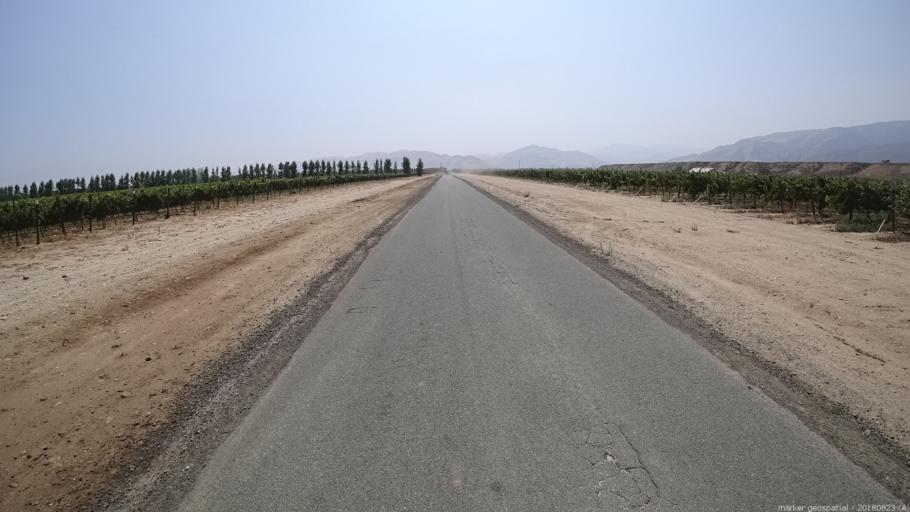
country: US
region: California
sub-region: Monterey County
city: Greenfield
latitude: 36.3306
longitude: -121.2963
